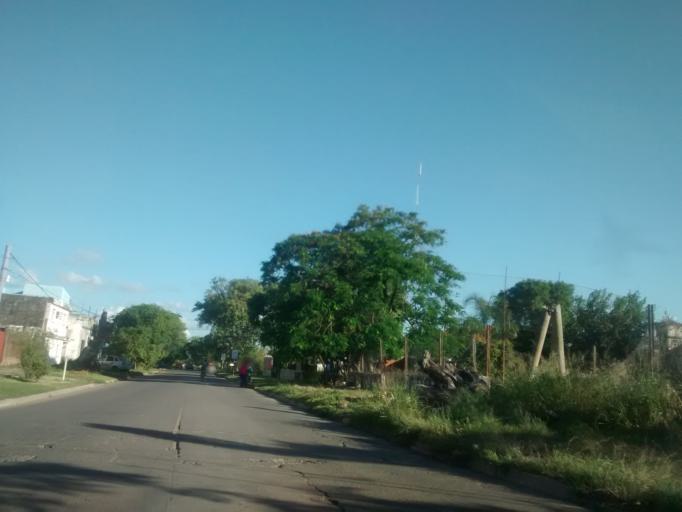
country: AR
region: Chaco
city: Resistencia
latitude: -27.4625
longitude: -58.9815
